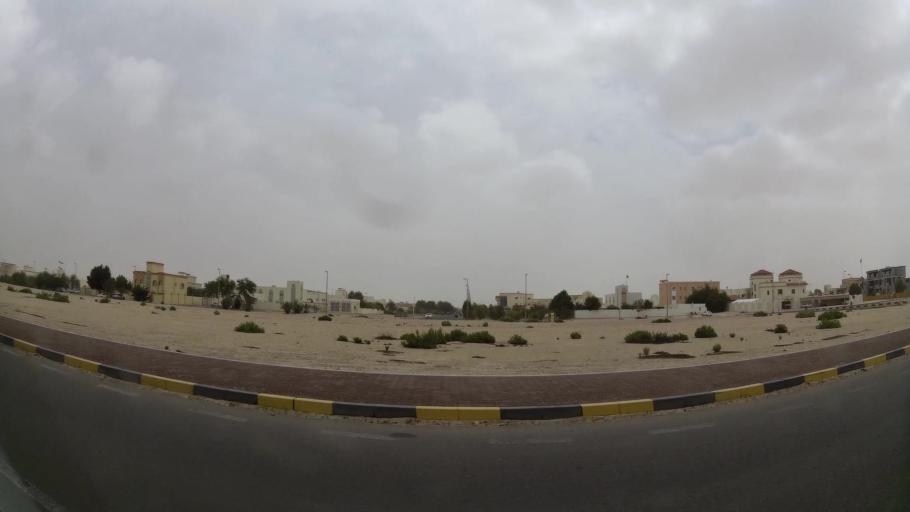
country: AE
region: Abu Dhabi
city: Abu Dhabi
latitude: 24.3967
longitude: 54.7178
